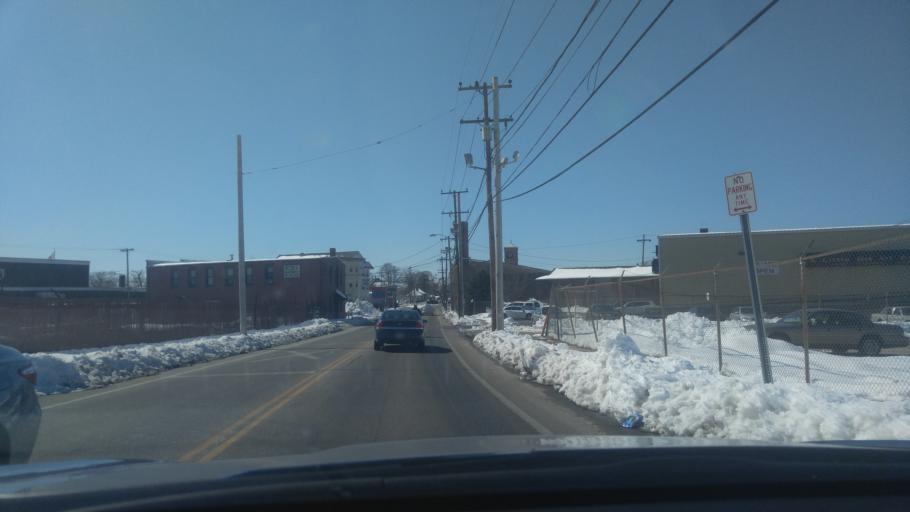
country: US
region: Rhode Island
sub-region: Providence County
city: Pawtucket
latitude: 41.8862
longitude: -71.3678
